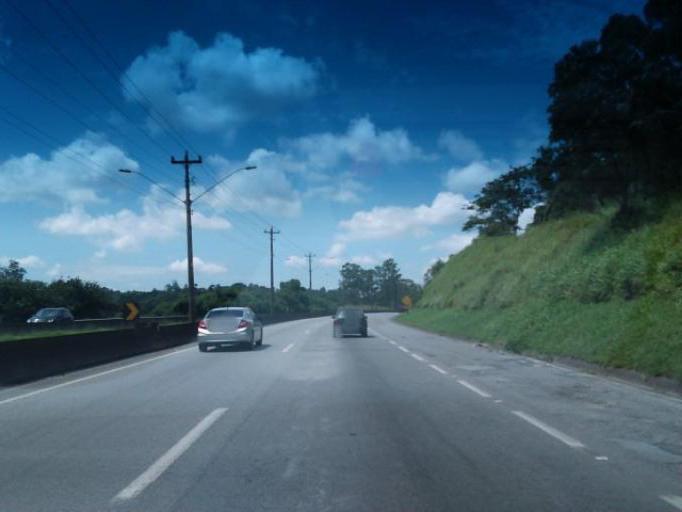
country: BR
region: Sao Paulo
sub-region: Itapecerica Da Serra
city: Itapecerica da Serra
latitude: -23.7571
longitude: -46.9026
